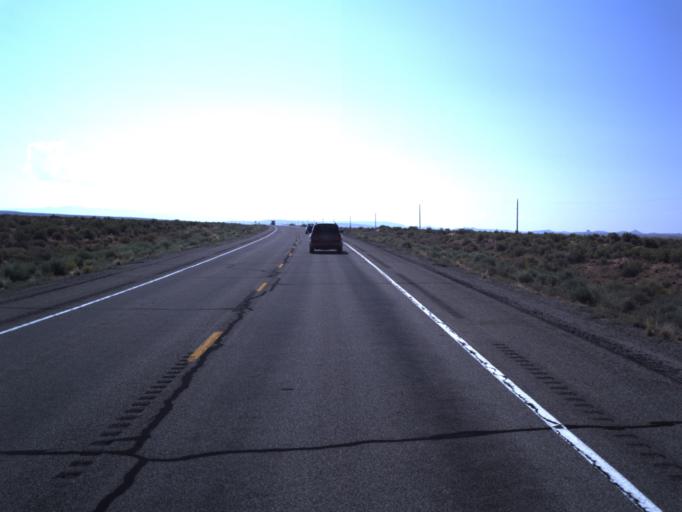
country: US
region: Utah
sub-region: San Juan County
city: Blanding
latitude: 37.2039
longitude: -109.6063
